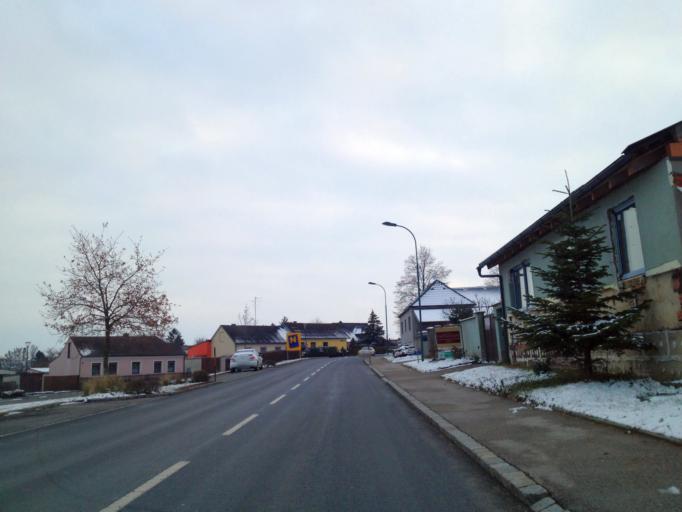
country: AT
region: Lower Austria
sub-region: Politischer Bezirk Bruck an der Leitha
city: Berg
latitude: 48.1058
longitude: 17.0435
